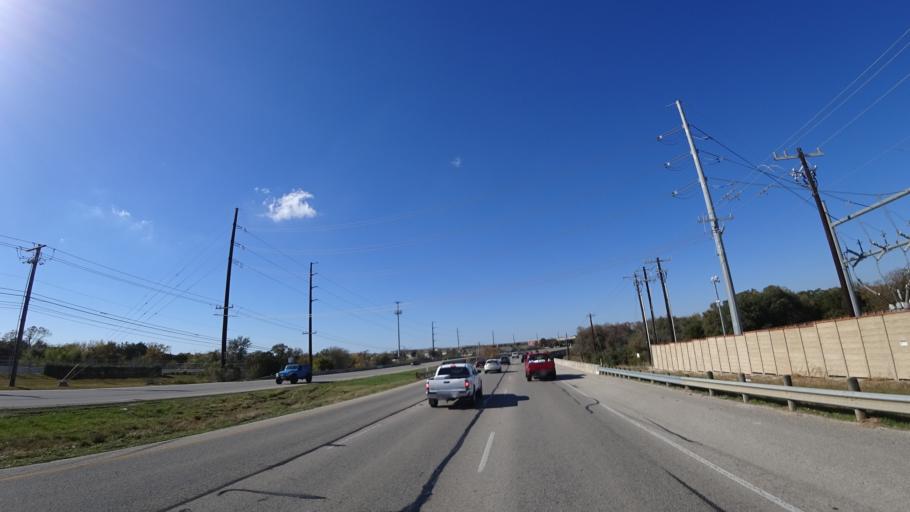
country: US
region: Texas
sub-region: Williamson County
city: Jollyville
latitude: 30.4641
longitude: -97.7575
